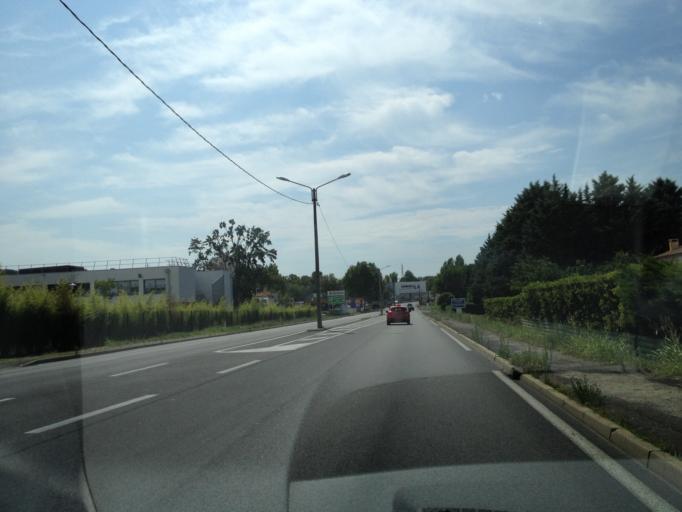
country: FR
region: Languedoc-Roussillon
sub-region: Departement du Gard
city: Ales
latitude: 44.1440
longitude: 4.1028
